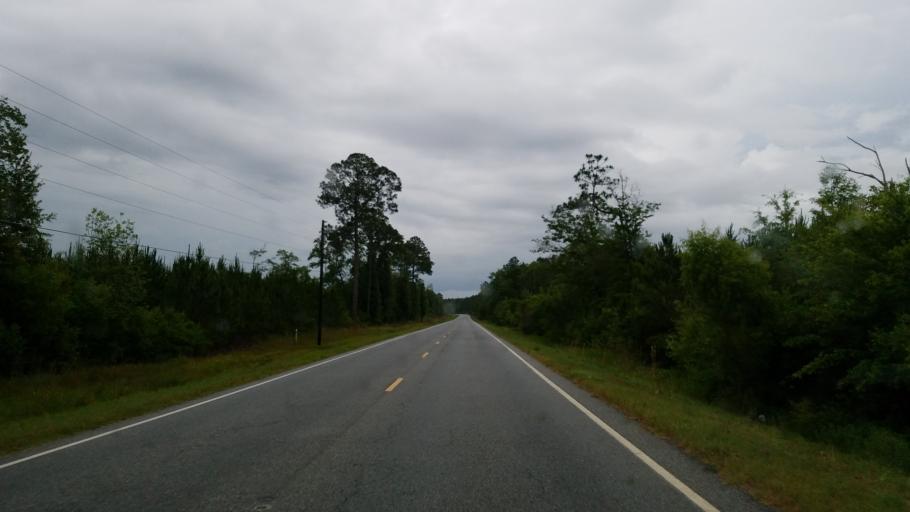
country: US
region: Georgia
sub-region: Berrien County
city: Ray City
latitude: 31.0571
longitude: -83.1485
